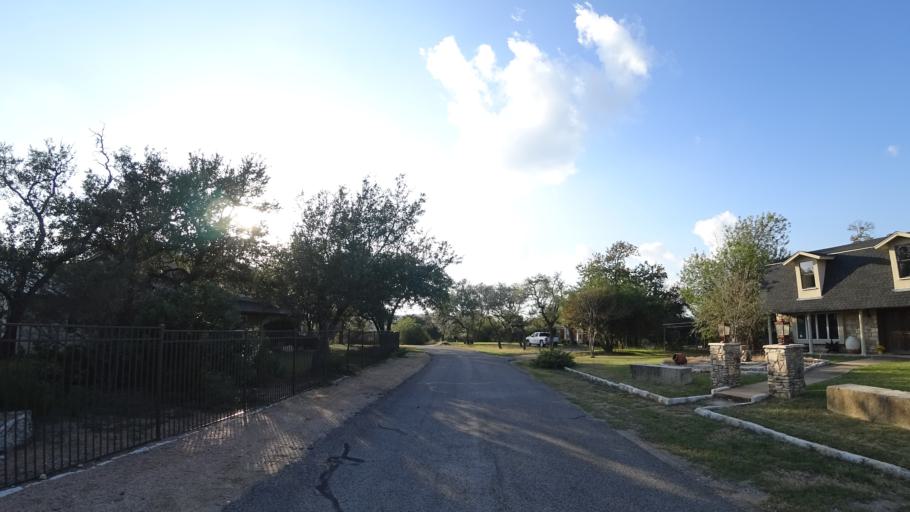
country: US
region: Texas
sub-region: Travis County
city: Lost Creek
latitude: 30.2955
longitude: -97.8475
